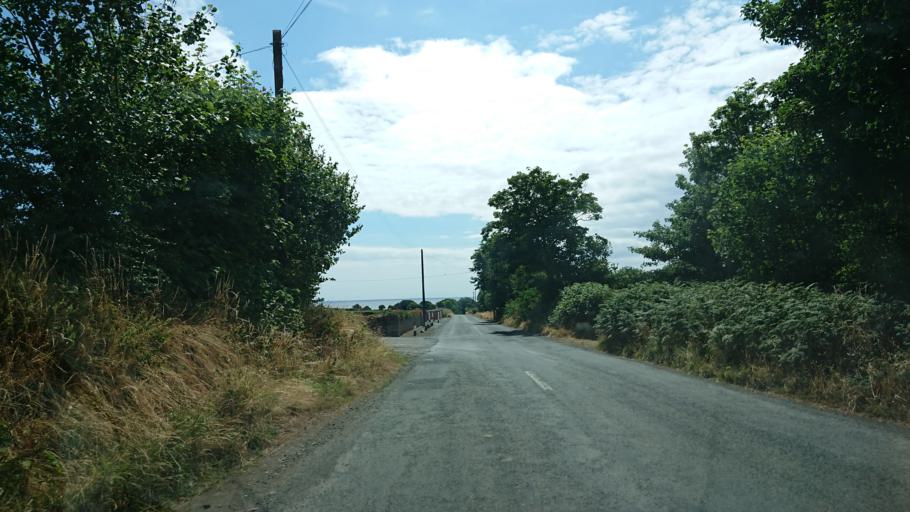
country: IE
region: Munster
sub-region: Waterford
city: Portlaw
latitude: 52.1494
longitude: -7.3534
